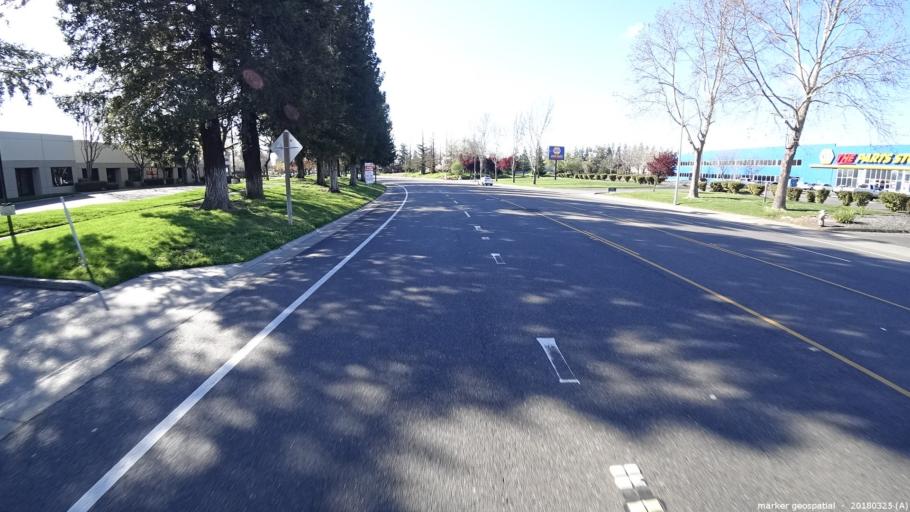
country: US
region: California
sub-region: Sacramento County
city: Rio Linda
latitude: 38.6535
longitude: -121.4781
